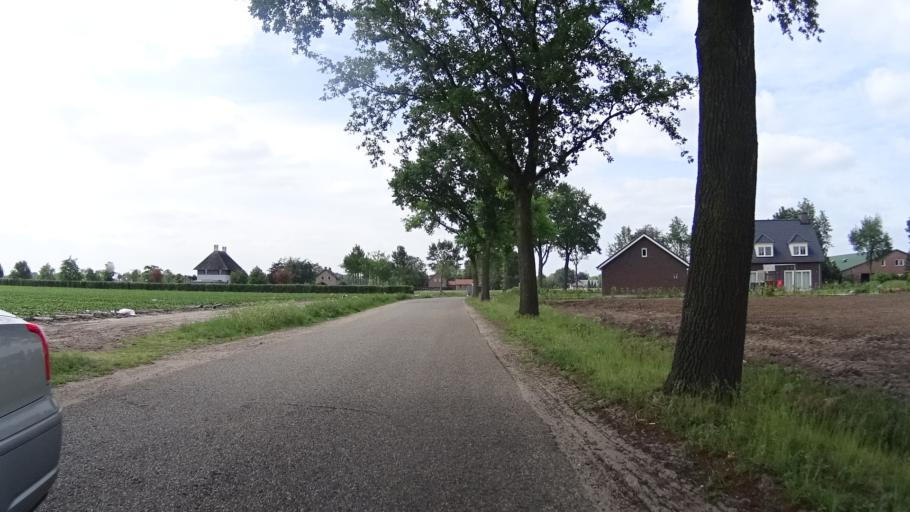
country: NL
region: North Brabant
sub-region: Gemeente Uden
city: Uden
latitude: 51.6350
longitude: 5.6171
